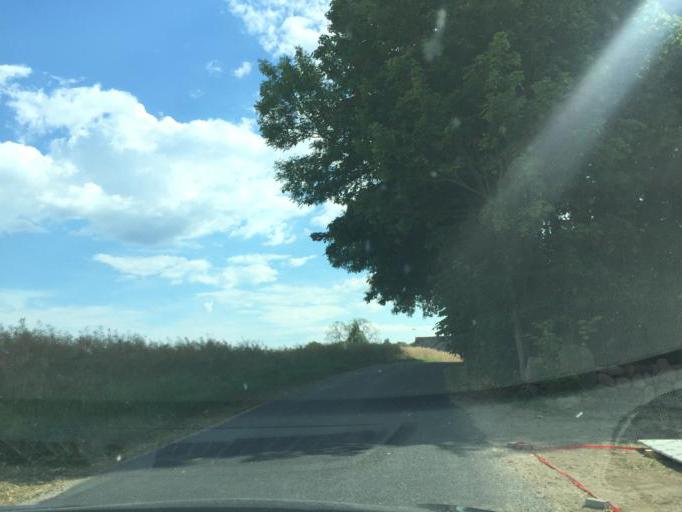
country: DK
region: South Denmark
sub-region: Assens Kommune
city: Harby
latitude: 55.1394
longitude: 10.0186
